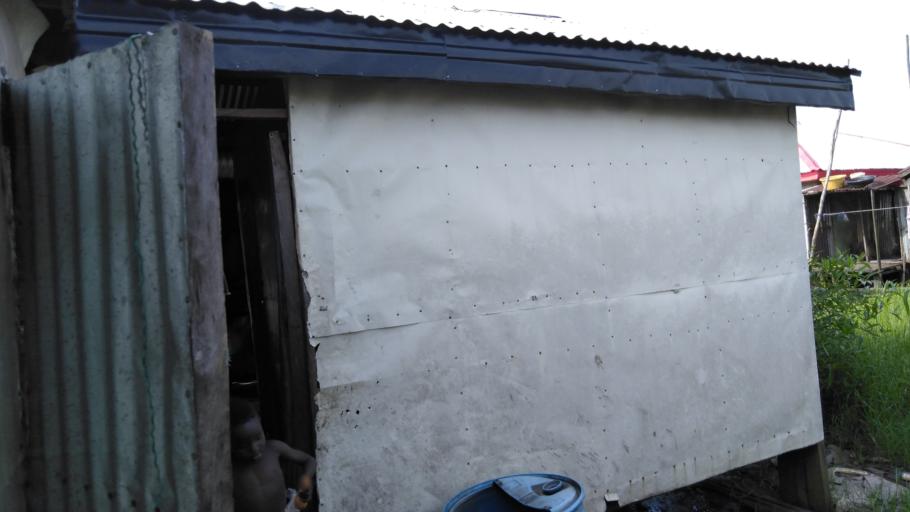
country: NG
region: Ondo
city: Igbekebo
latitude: 5.9273
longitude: 4.9611
